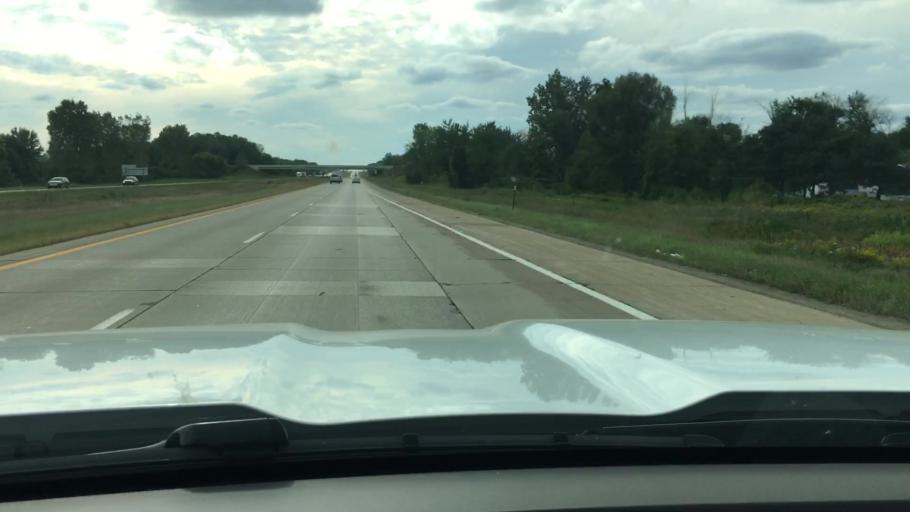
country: US
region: Michigan
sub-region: Lapeer County
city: Imlay City
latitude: 43.0003
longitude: -83.0778
